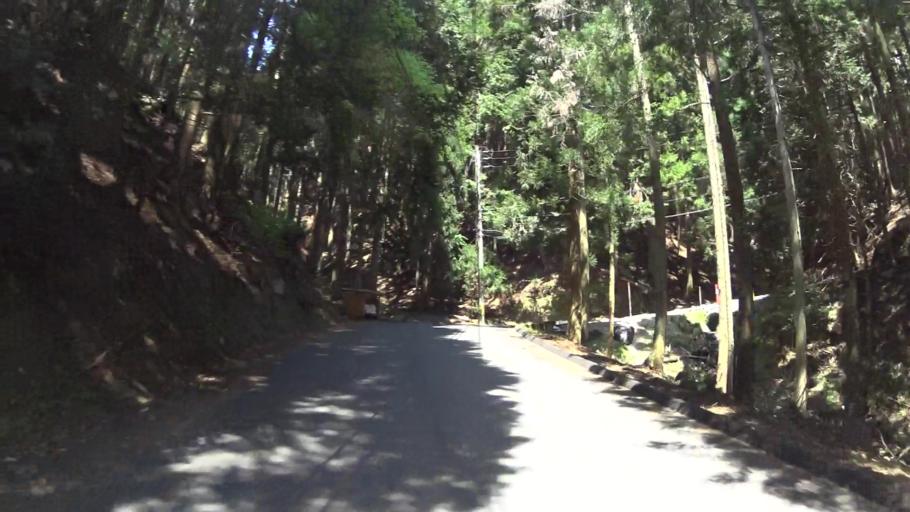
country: JP
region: Shiga Prefecture
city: Kitahama
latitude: 35.1565
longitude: 135.8057
